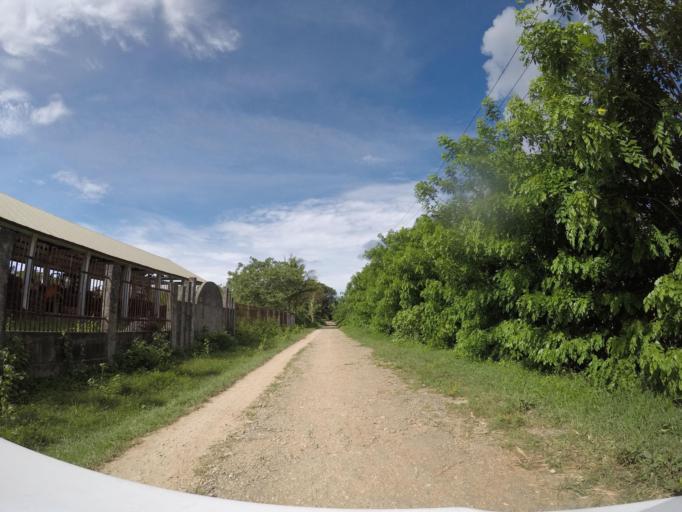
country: TL
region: Lautem
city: Lospalos
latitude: -8.4959
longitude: 126.9935
